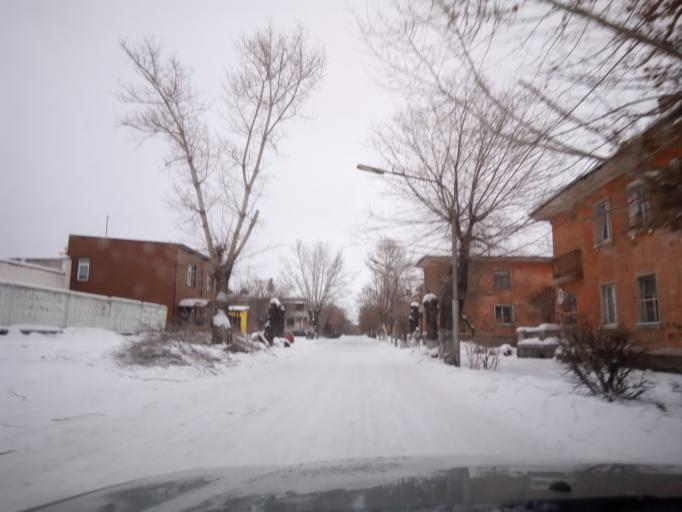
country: RU
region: Orenburg
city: Novotroitsk
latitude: 51.1974
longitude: 58.3233
